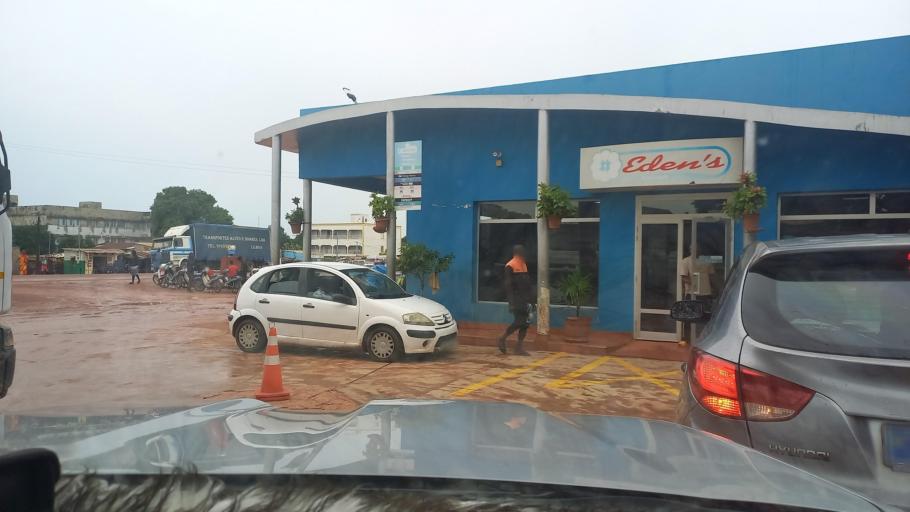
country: SN
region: Ziguinchor
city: Ziguinchor
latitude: 12.5628
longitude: -16.2659
